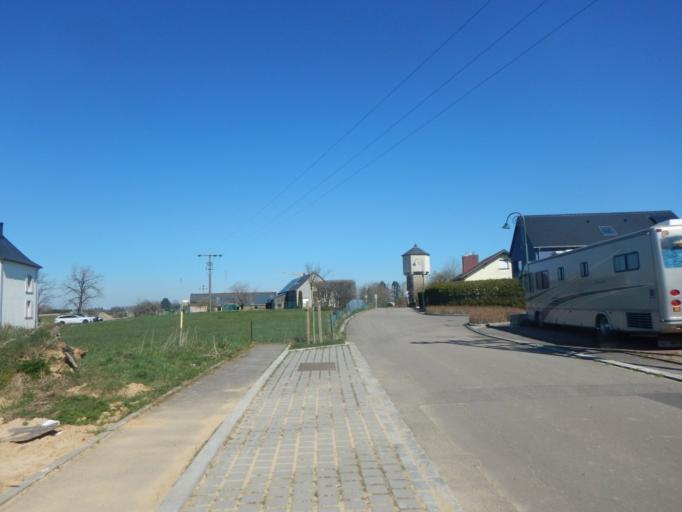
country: LU
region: Luxembourg
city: Schouweiler
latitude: 49.5977
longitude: 5.9439
